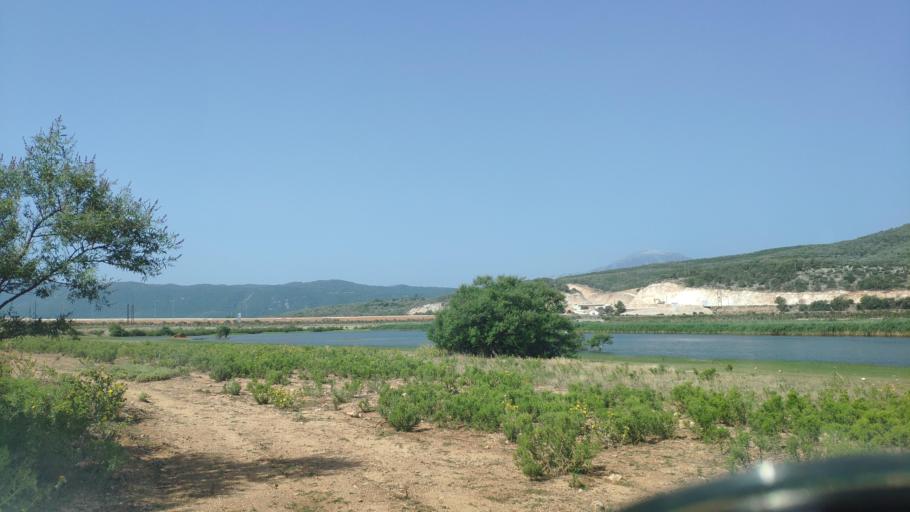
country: GR
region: West Greece
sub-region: Nomos Aitolias kai Akarnanias
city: Stanos
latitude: 38.7812
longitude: 21.1917
